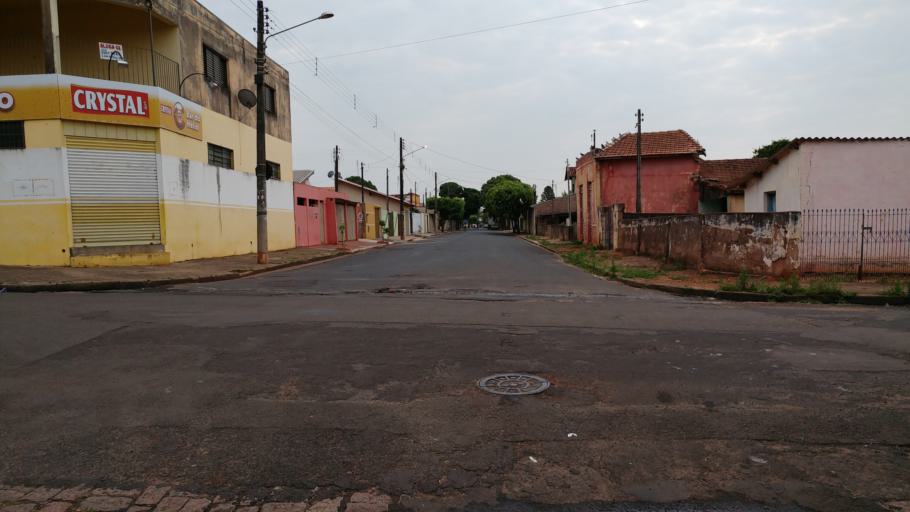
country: BR
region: Sao Paulo
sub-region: Paraguacu Paulista
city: Paraguacu Paulista
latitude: -22.4166
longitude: -50.5708
